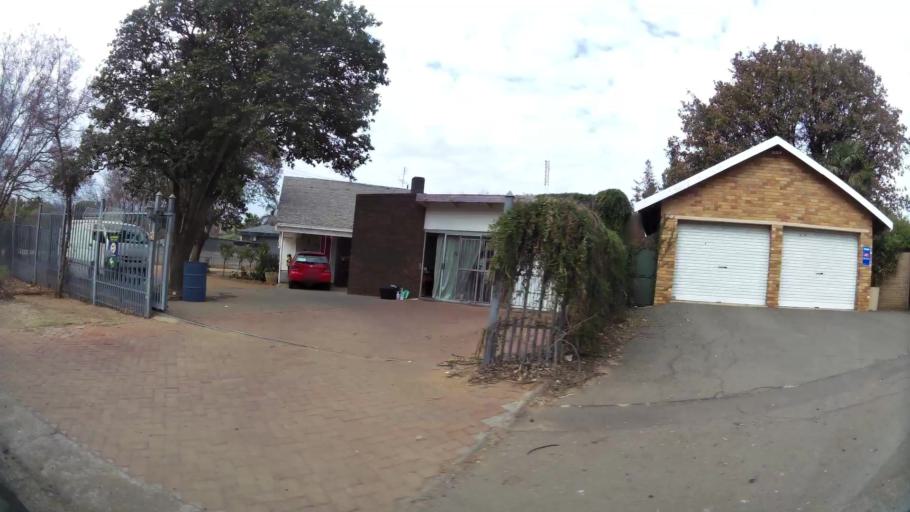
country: ZA
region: Orange Free State
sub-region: Mangaung Metropolitan Municipality
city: Bloemfontein
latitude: -29.0974
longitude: 26.2127
